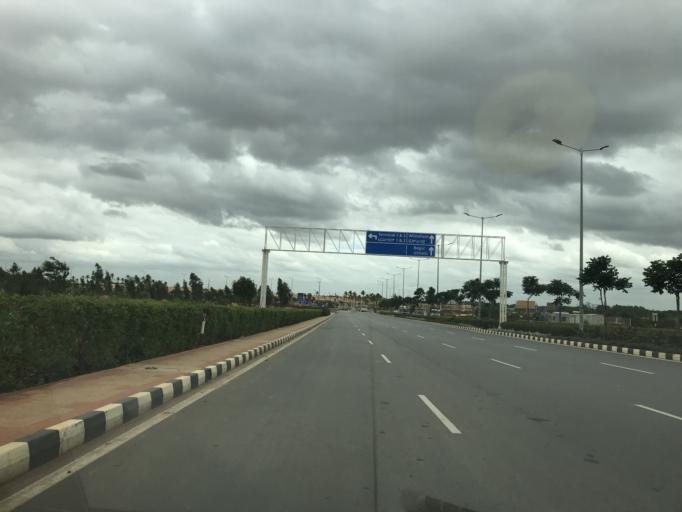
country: IN
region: Karnataka
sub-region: Bangalore Rural
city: Devanhalli
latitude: 13.1969
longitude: 77.6802
